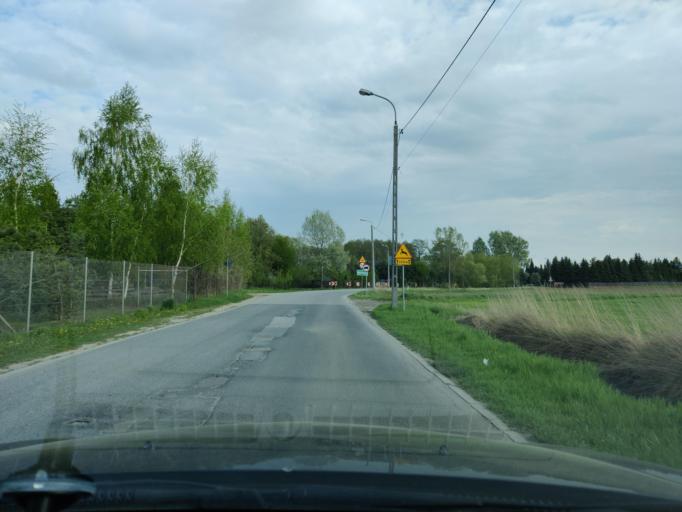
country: PL
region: Masovian Voivodeship
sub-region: Powiat piaseczynski
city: Konstancin-Jeziorna
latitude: 52.1302
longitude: 21.1376
